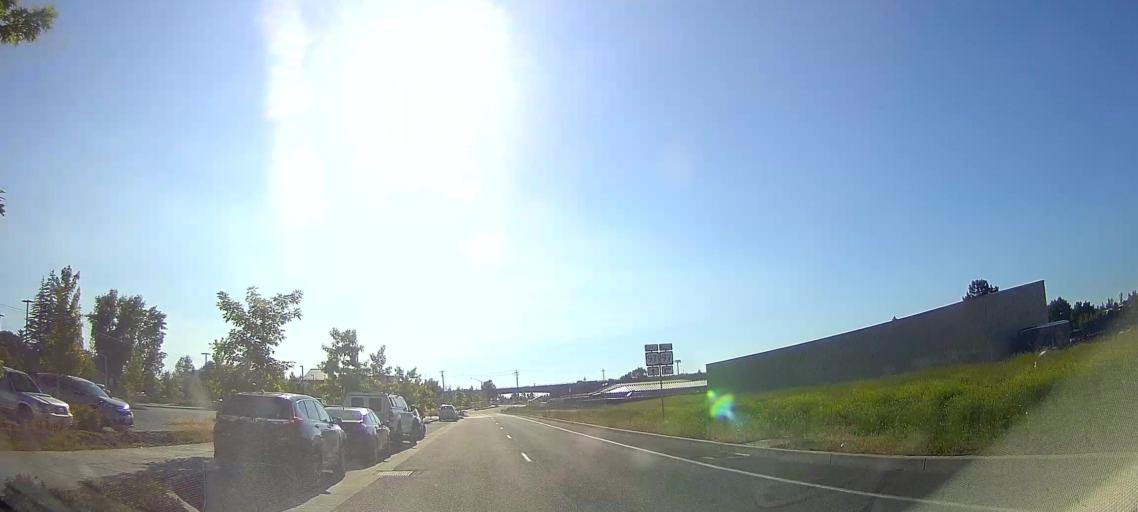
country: US
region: Oregon
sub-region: Deschutes County
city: Bend
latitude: 44.0518
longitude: -121.3126
